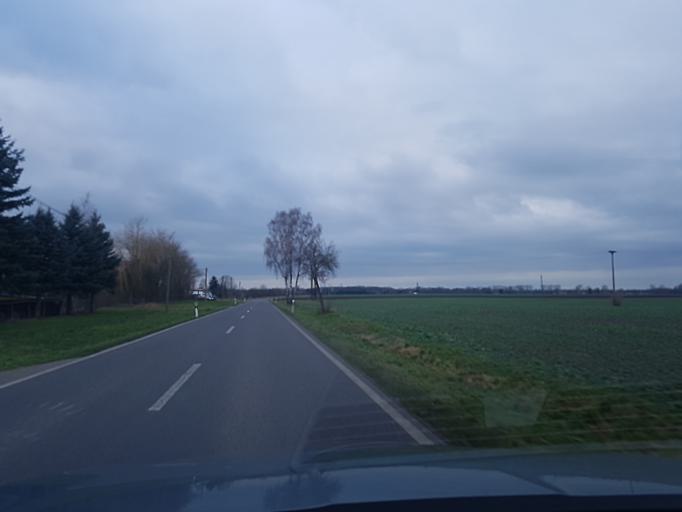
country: DE
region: Brandenburg
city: Sonnewalde
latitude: 51.6915
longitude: 13.6722
